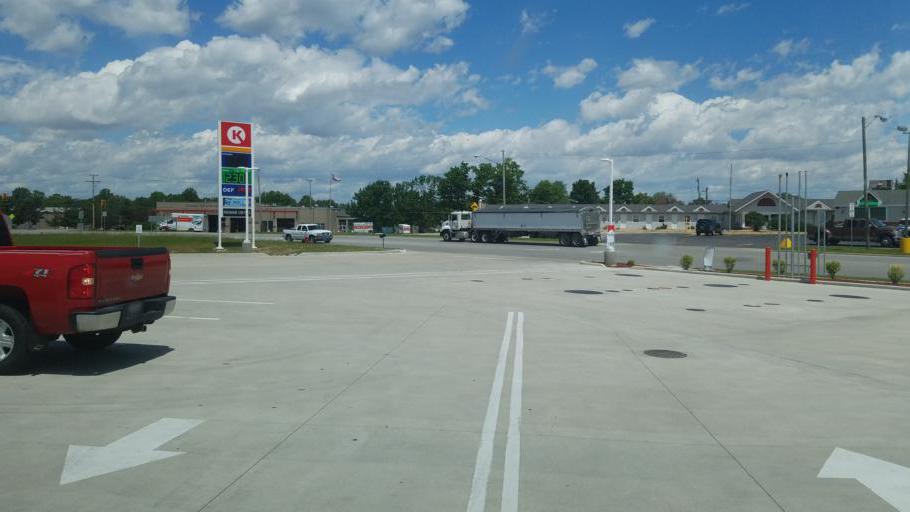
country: US
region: Ohio
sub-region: Huron County
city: Willard
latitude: 41.0413
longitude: -82.7172
